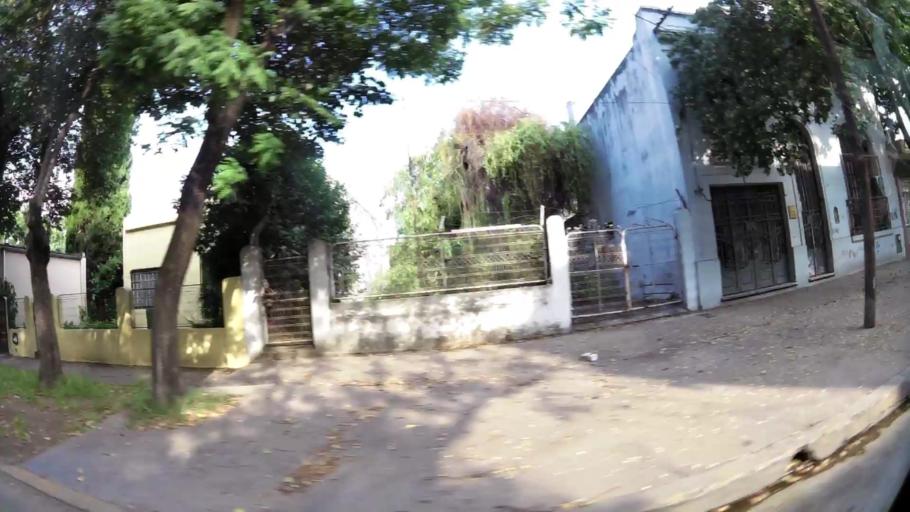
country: AR
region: Buenos Aires
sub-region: Partido de Merlo
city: Merlo
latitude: -34.6689
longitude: -58.7213
